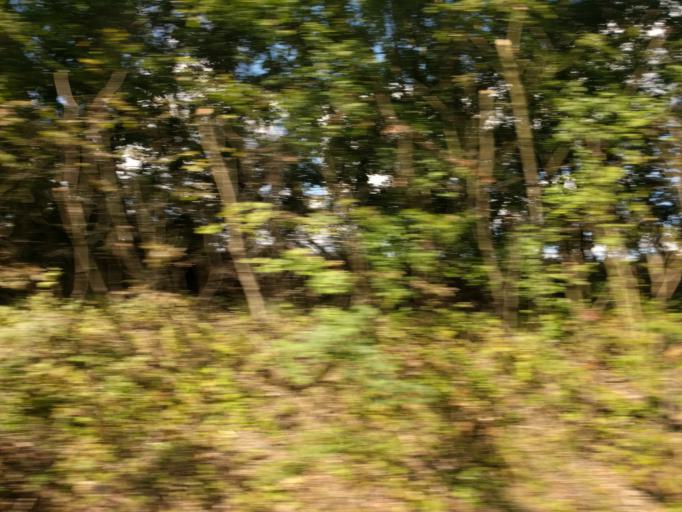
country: DK
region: Zealand
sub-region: Roskilde Kommune
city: Viby
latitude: 55.5358
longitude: 12.0022
